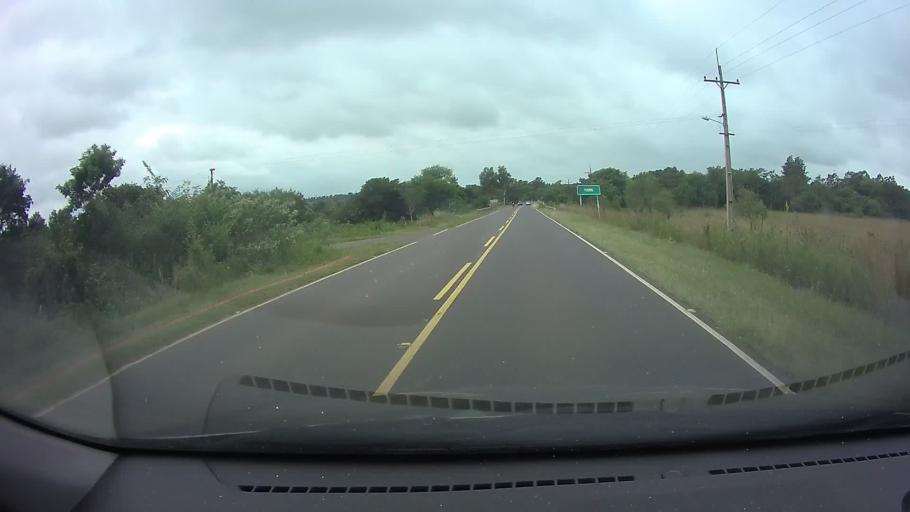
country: PY
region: Central
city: Nueva Italia
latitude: -25.6120
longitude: -57.4449
